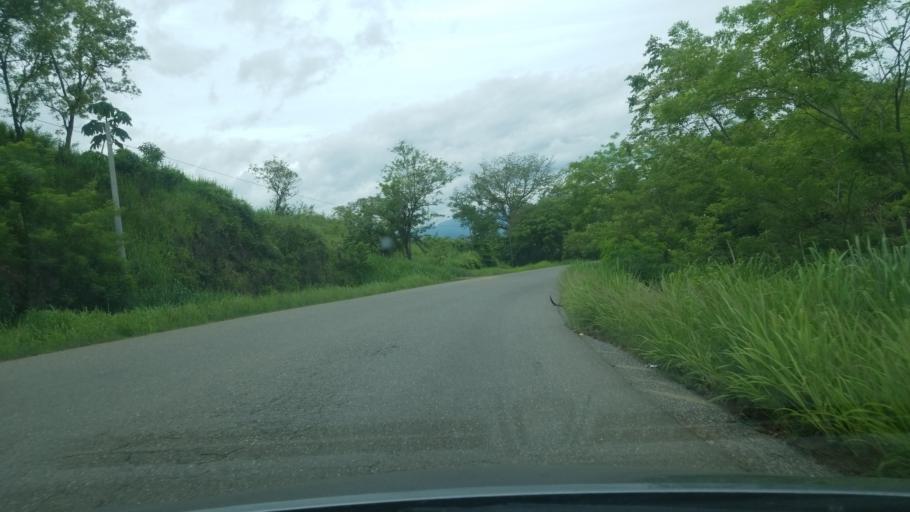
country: HN
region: Santa Barbara
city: La Flecha
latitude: 15.2967
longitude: -88.4580
